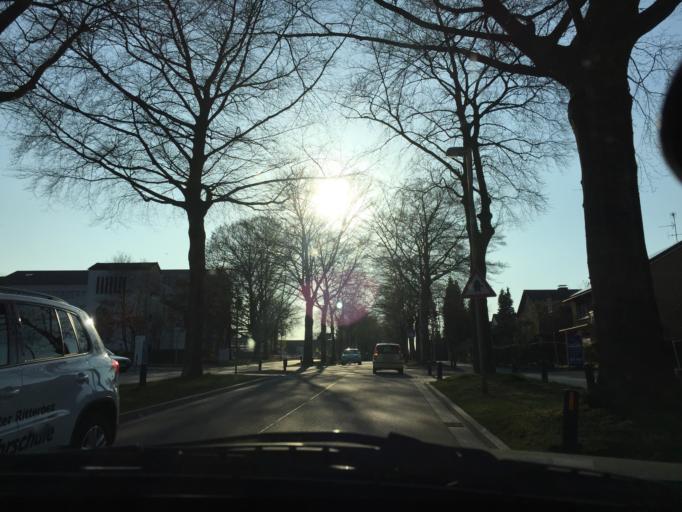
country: DE
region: North Rhine-Westphalia
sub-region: Regierungsbezirk Dusseldorf
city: Kleve
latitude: 51.7738
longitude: 6.1377
